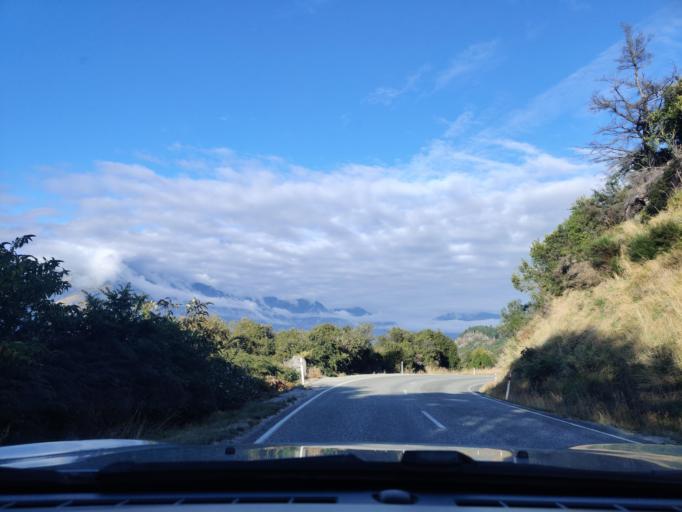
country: NZ
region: Otago
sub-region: Queenstown-Lakes District
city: Queenstown
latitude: -45.0565
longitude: 168.5998
